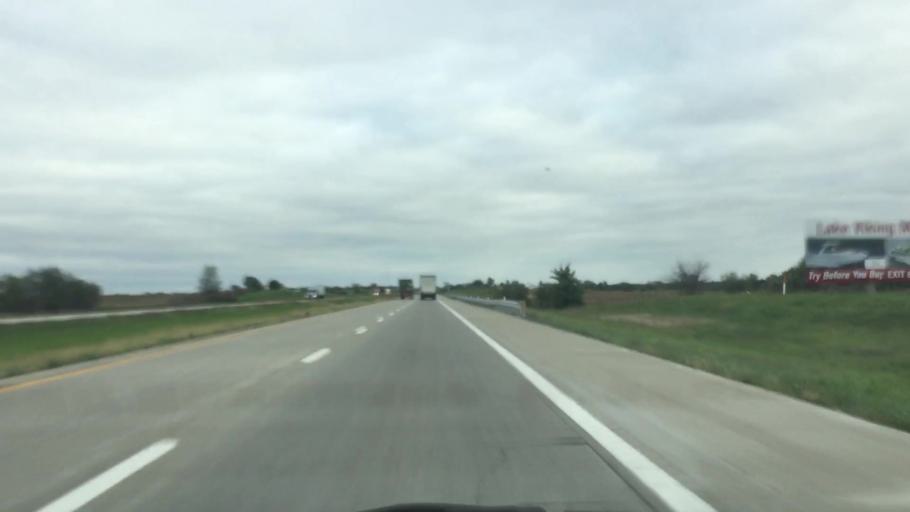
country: US
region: Missouri
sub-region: Clinton County
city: Lathrop
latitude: 39.5775
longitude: -94.2600
